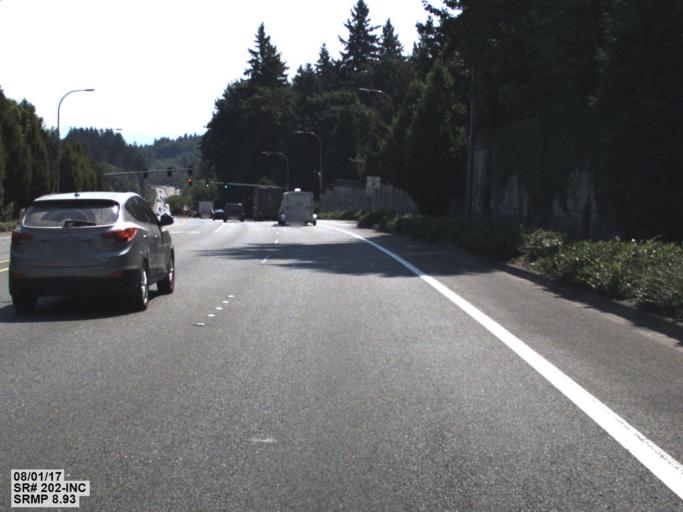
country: US
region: Washington
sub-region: King County
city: Sammamish
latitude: 47.6580
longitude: -122.0904
